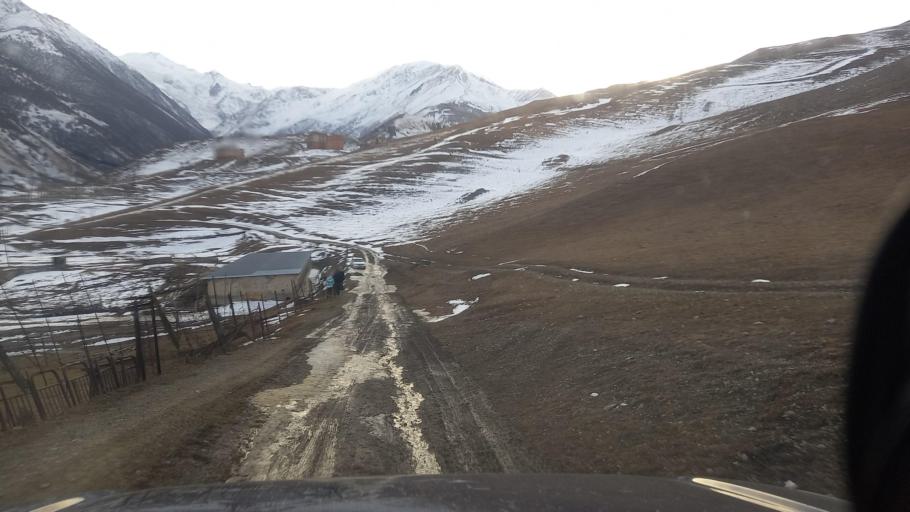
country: RU
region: Ingushetiya
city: Dzhayrakh
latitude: 42.8505
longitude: 44.5135
